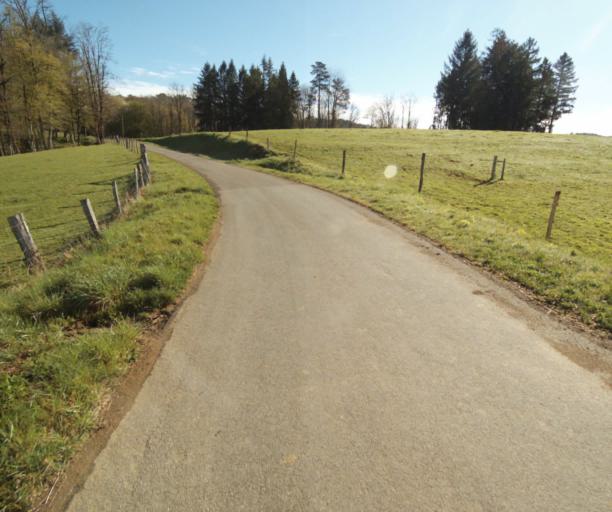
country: FR
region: Limousin
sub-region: Departement de la Correze
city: Laguenne
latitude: 45.2577
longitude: 1.8429
